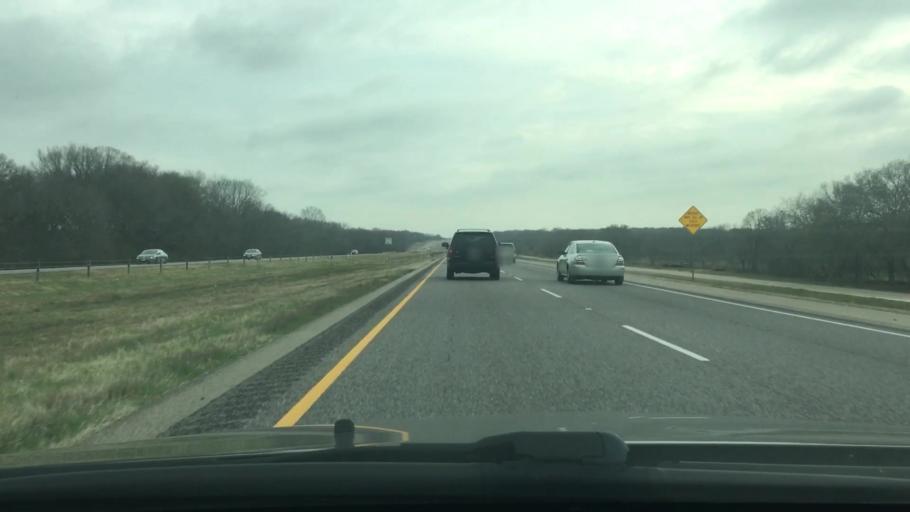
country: US
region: Texas
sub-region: Freestone County
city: Fairfield
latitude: 31.6537
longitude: -96.1607
